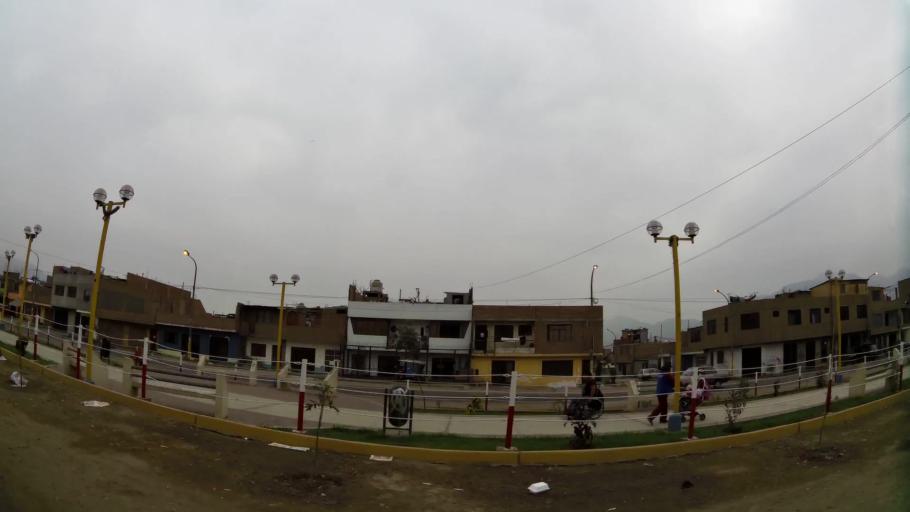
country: PE
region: Lima
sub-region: Lima
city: Independencia
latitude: -11.9654
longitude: -76.9977
